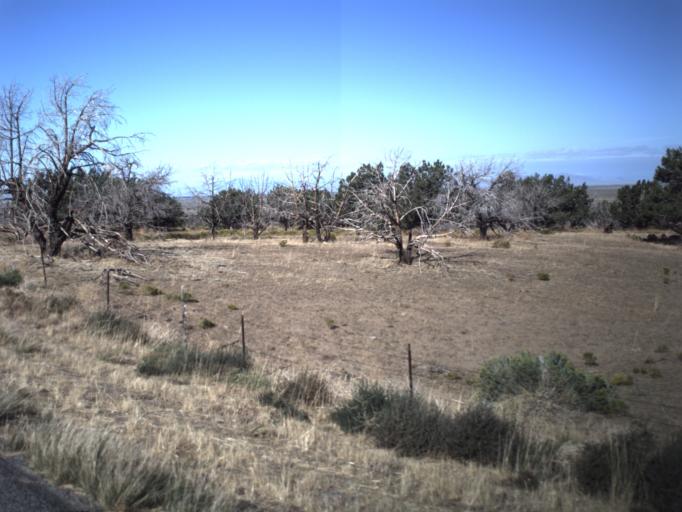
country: US
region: Utah
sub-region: Millard County
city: Delta
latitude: 39.3605
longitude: -112.3539
